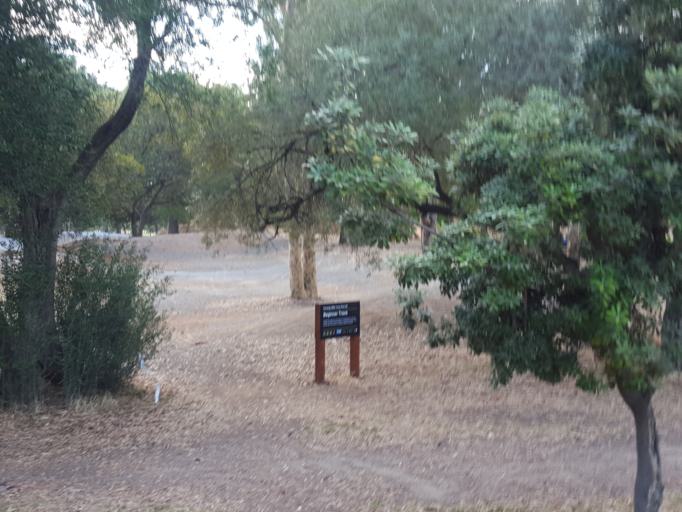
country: AU
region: South Australia
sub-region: Adelaide
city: Adelaide
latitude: -34.9388
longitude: 138.6065
